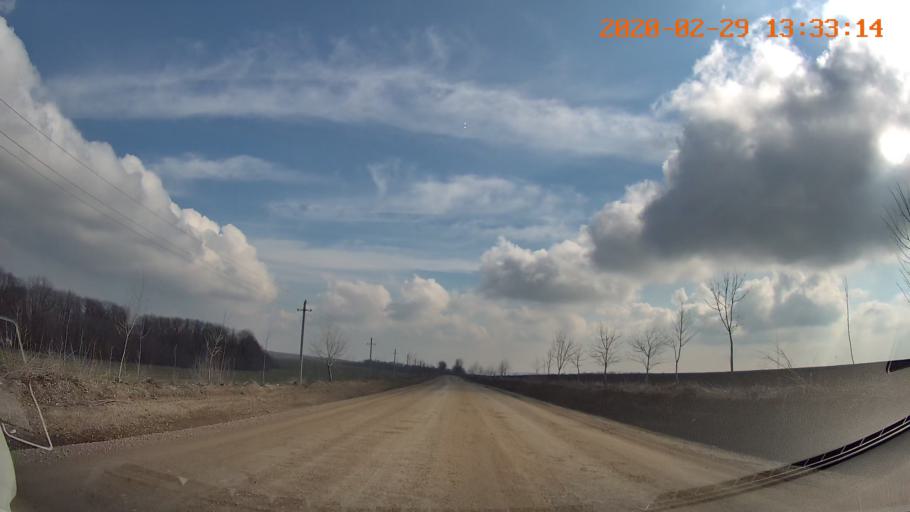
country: MD
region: Telenesti
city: Camenca
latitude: 47.8746
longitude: 28.6151
